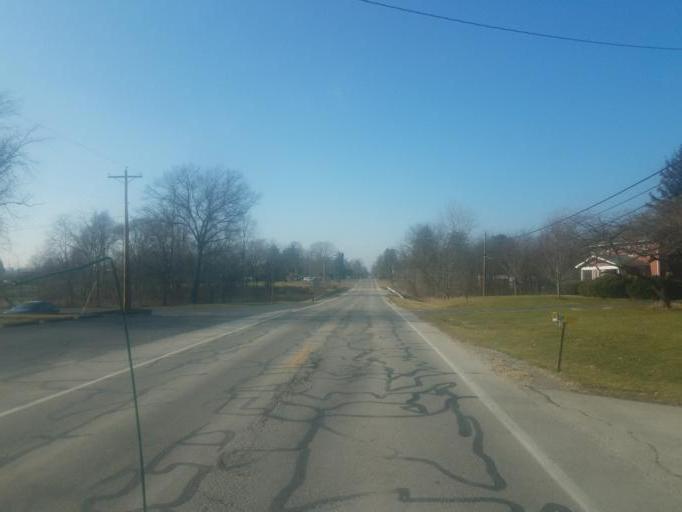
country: US
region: Ohio
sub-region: Seneca County
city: Tiffin
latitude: 41.1205
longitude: -83.1544
